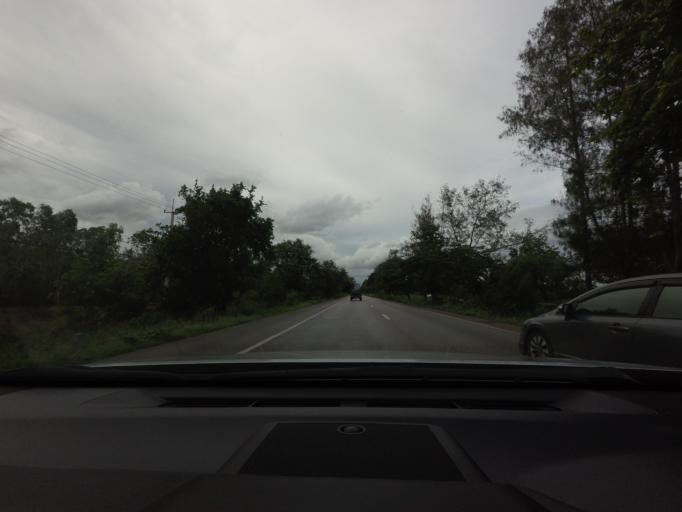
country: TH
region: Phetchaburi
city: Cha-am
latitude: 12.7358
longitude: 99.9282
